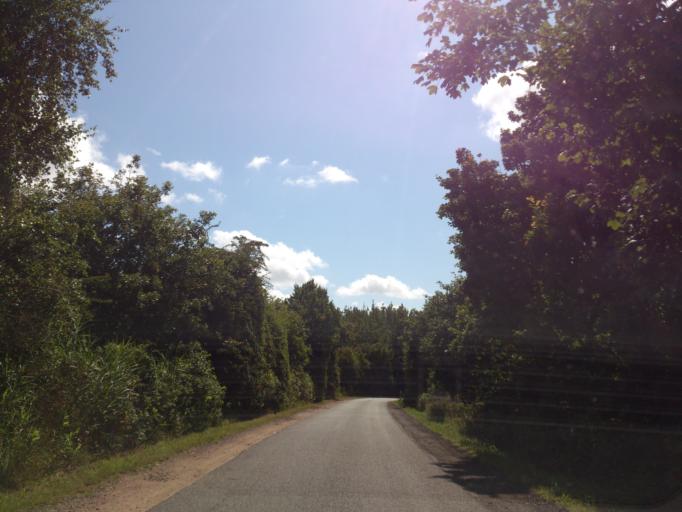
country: DE
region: Schleswig-Holstein
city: Sankt Peter-Ording
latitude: 54.3125
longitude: 8.6311
